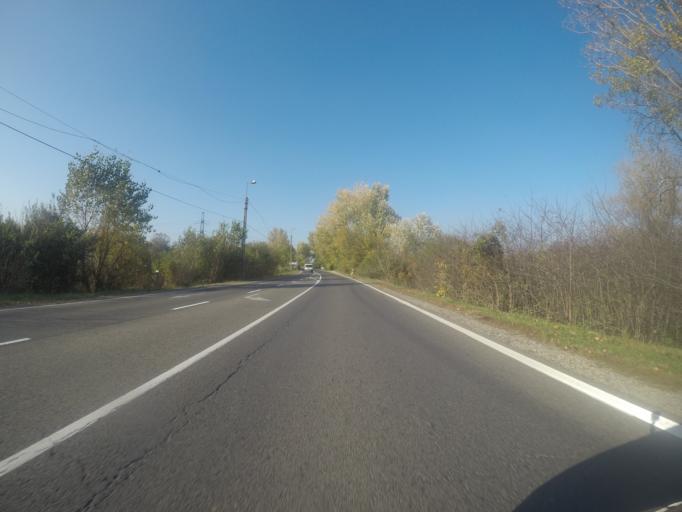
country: HU
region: Fejer
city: Ercsi
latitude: 47.2615
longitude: 18.8940
